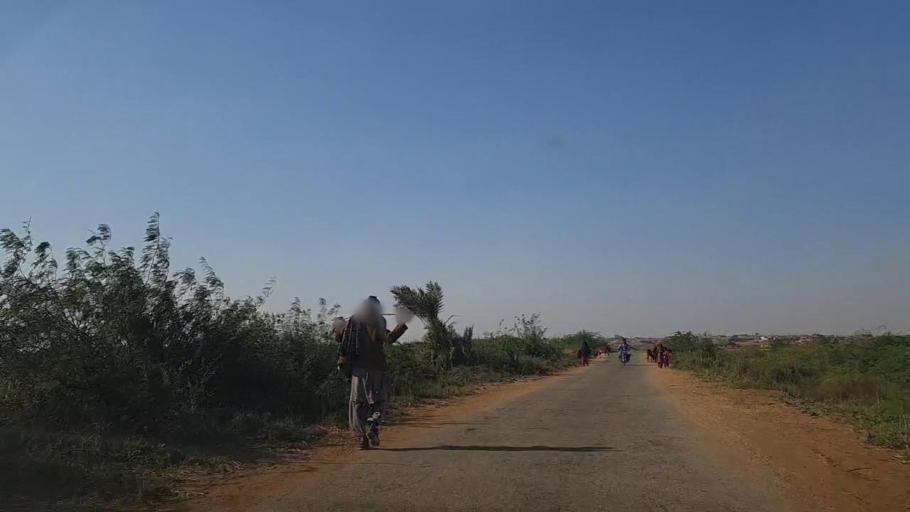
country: PK
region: Sindh
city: Daro Mehar
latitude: 24.9866
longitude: 68.1326
